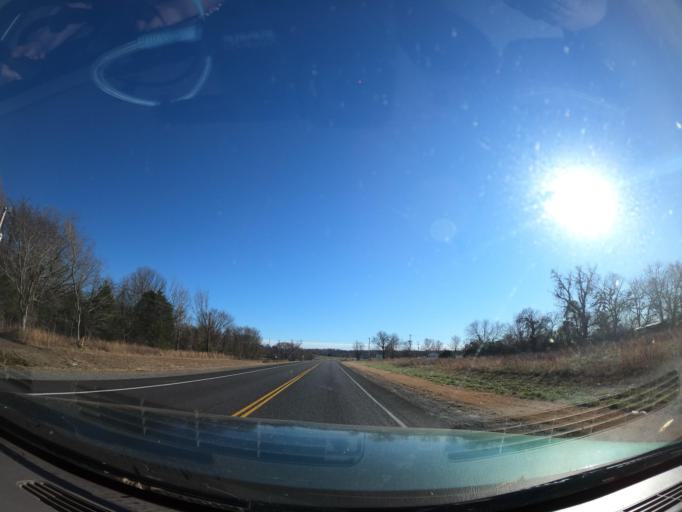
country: US
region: Oklahoma
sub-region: McIntosh County
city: Eufaula
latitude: 35.2621
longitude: -95.5799
